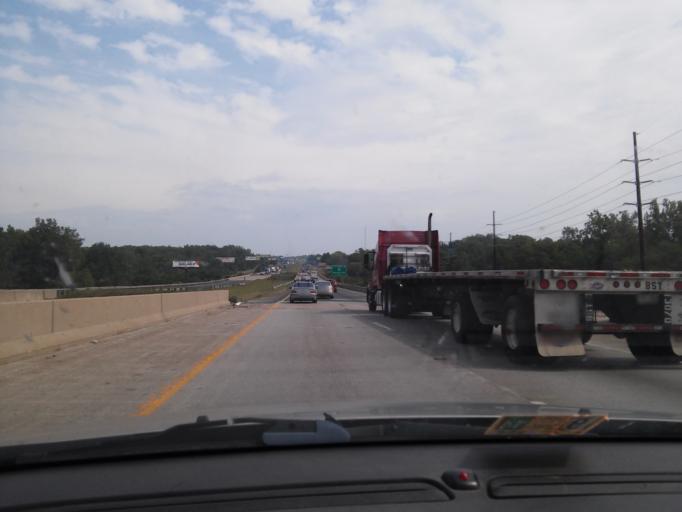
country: US
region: Ohio
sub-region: Preble County
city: New Paris
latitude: 39.8494
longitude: -84.8342
